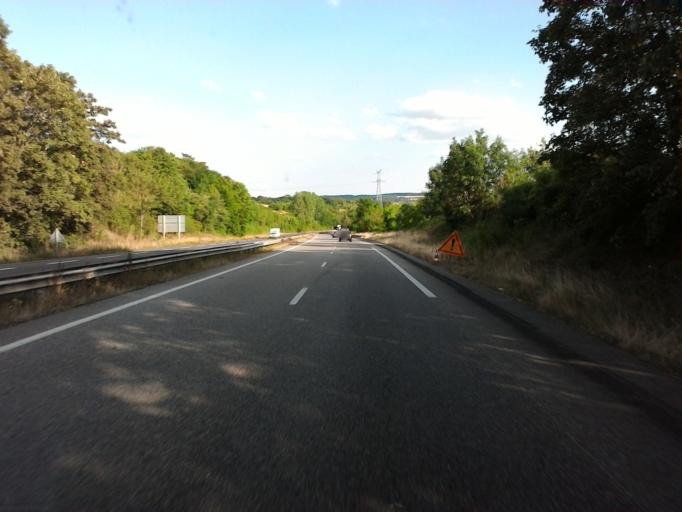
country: FR
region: Lorraine
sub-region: Departement de Meurthe-et-Moselle
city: Richardmenil
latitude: 48.5898
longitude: 6.1735
